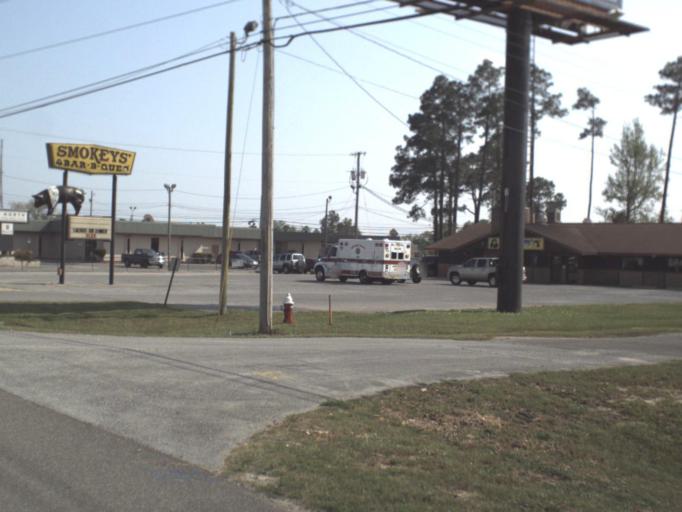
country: US
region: Florida
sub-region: Escambia County
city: Brent
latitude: 30.4835
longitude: -87.2569
